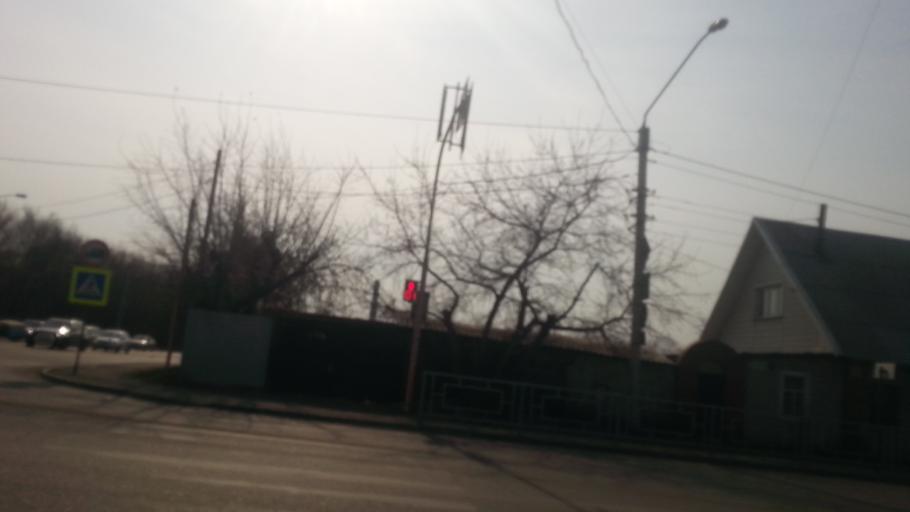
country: RU
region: Altai Krai
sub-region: Gorod Barnaulskiy
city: Barnaul
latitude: 53.3233
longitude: 83.7674
